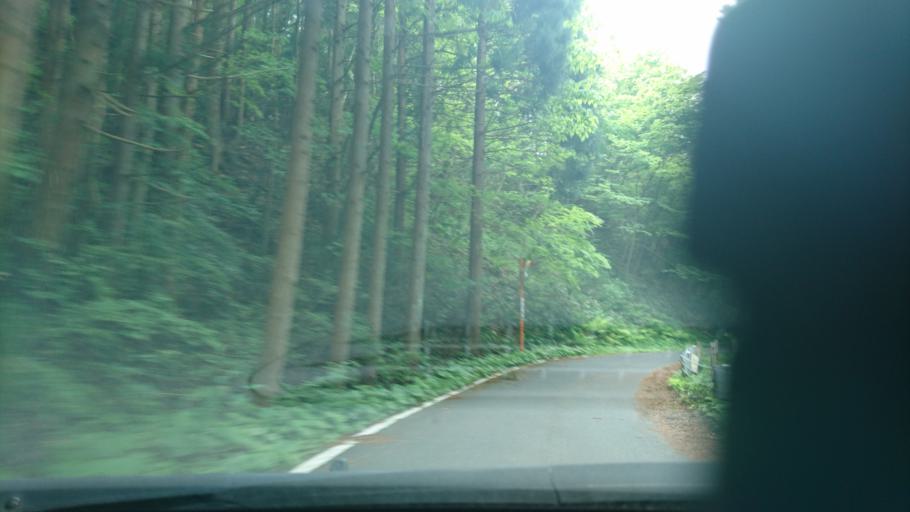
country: JP
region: Iwate
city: Ichinoseki
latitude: 38.9050
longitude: 140.9136
